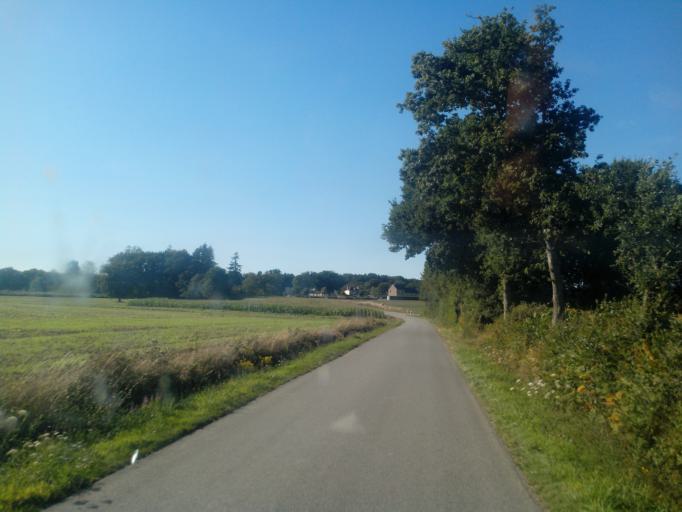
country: FR
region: Brittany
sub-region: Departement du Morbihan
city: Guilliers
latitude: 48.1169
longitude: -2.3846
